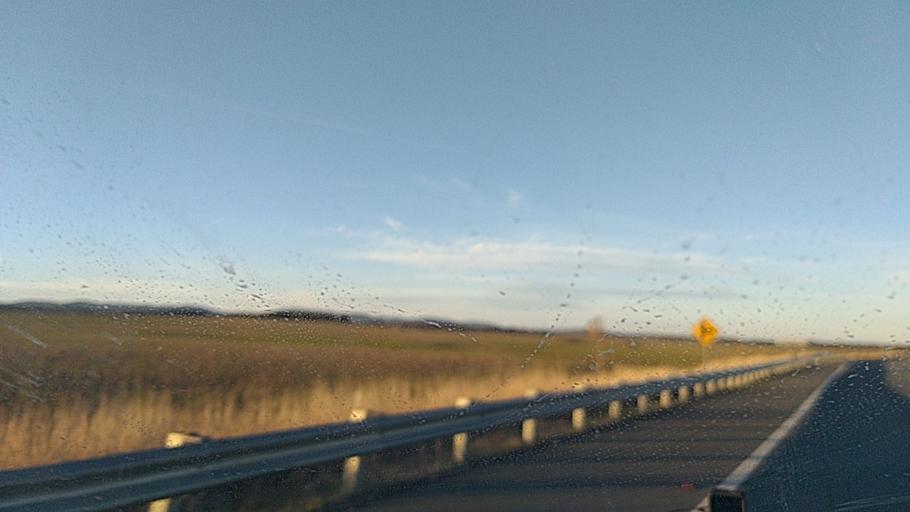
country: AU
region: New South Wales
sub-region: Goulburn Mulwaree
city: Goulburn
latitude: -34.8510
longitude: 149.5548
